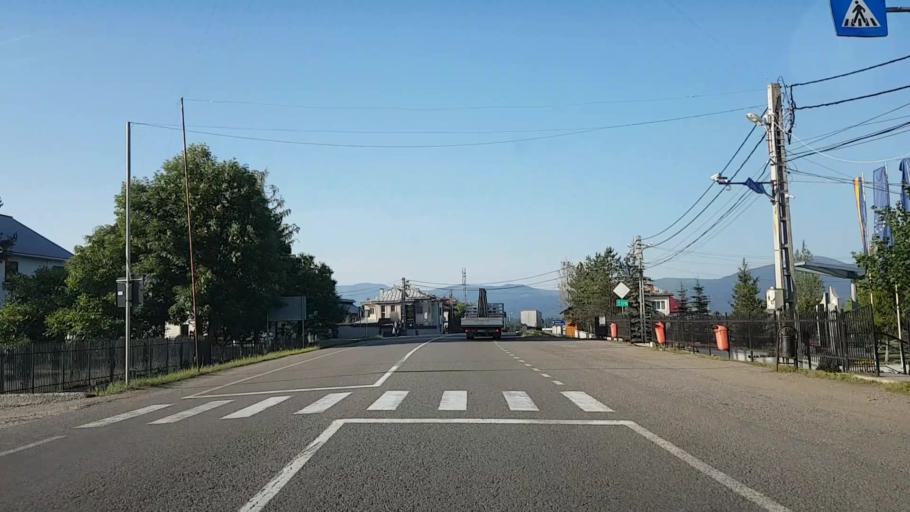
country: RO
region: Suceava
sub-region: Comuna Poiana Stampei
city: Poiana Stampei
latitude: 47.3236
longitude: 25.1396
